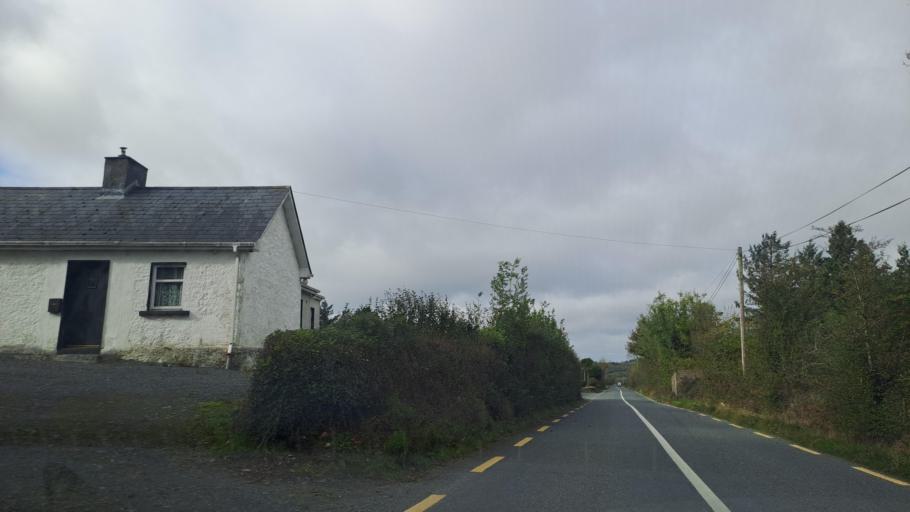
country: IE
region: Ulster
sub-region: An Cabhan
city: Bailieborough
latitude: 53.9308
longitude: -6.8959
